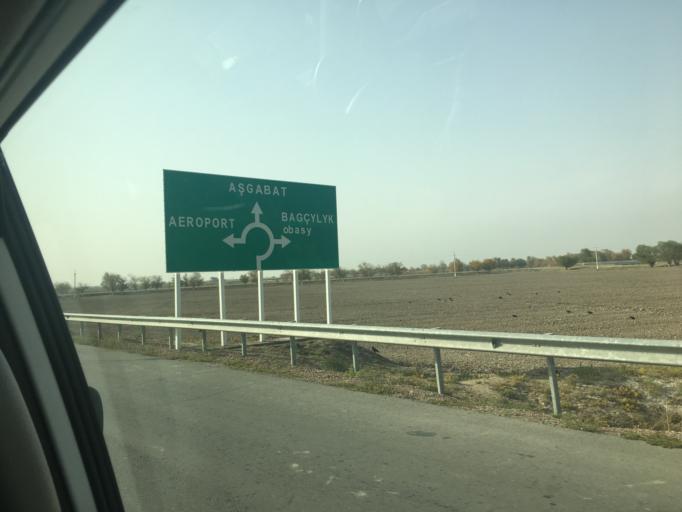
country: TM
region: Dasoguz
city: Dasoguz
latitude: 41.7737
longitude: 59.8368
